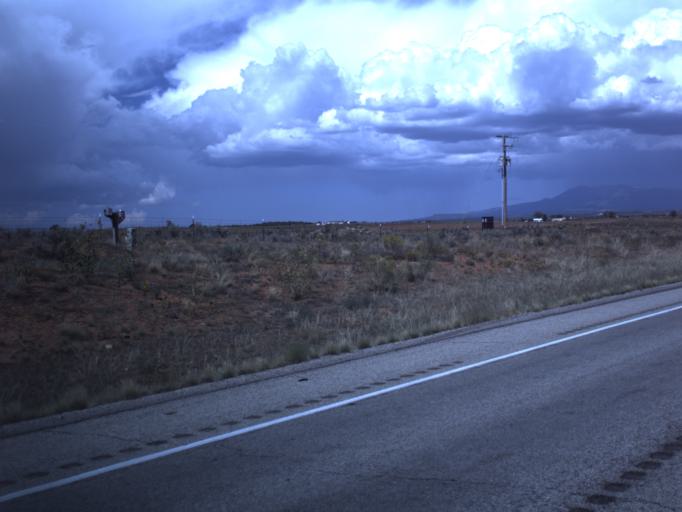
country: US
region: Utah
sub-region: San Juan County
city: Blanding
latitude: 37.5509
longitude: -109.4905
